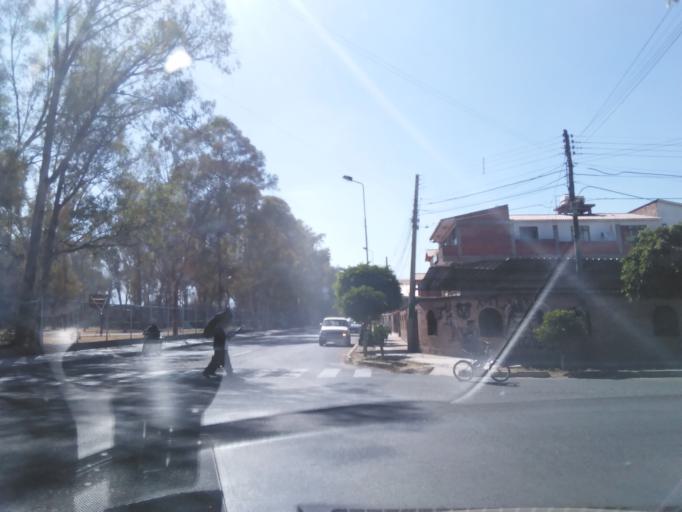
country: BO
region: Cochabamba
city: Cochabamba
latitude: -17.4024
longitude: -66.1743
